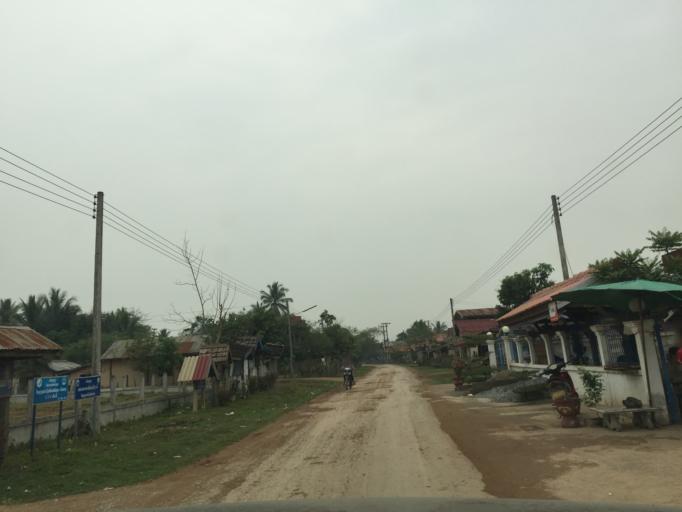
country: LA
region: Xiagnabouli
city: Sainyabuli
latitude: 19.0863
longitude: 101.5340
